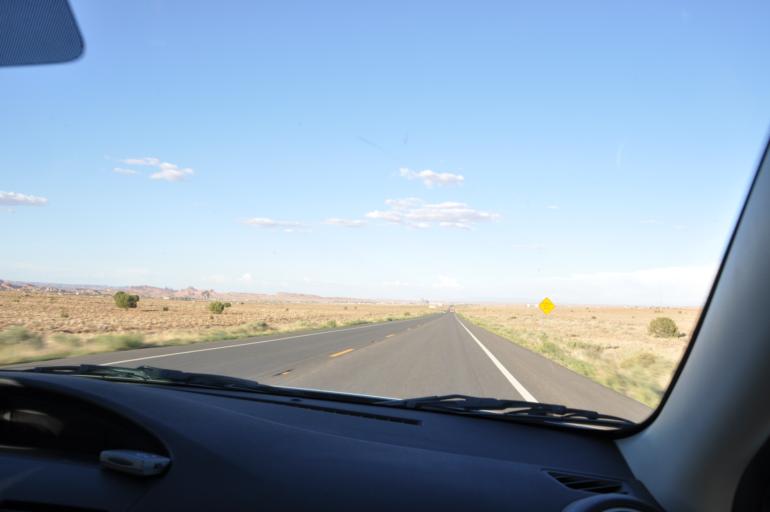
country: US
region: Arizona
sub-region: Navajo County
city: Kayenta
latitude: 36.7056
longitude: -110.2612
